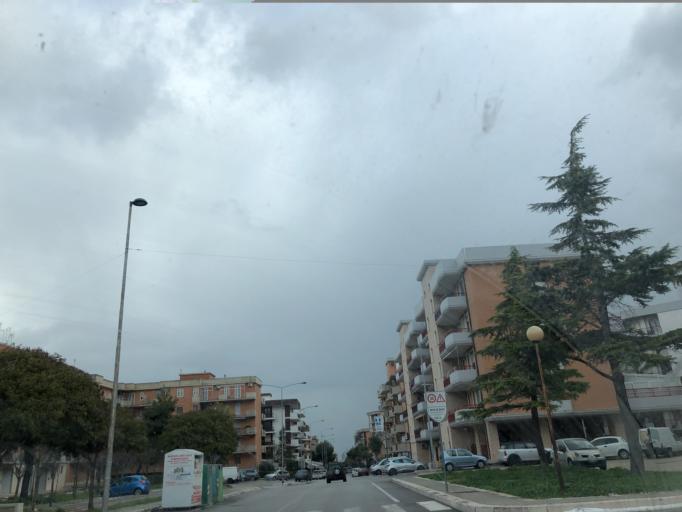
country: IT
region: Apulia
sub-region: Provincia di Foggia
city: Lucera
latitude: 41.5018
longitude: 15.3451
